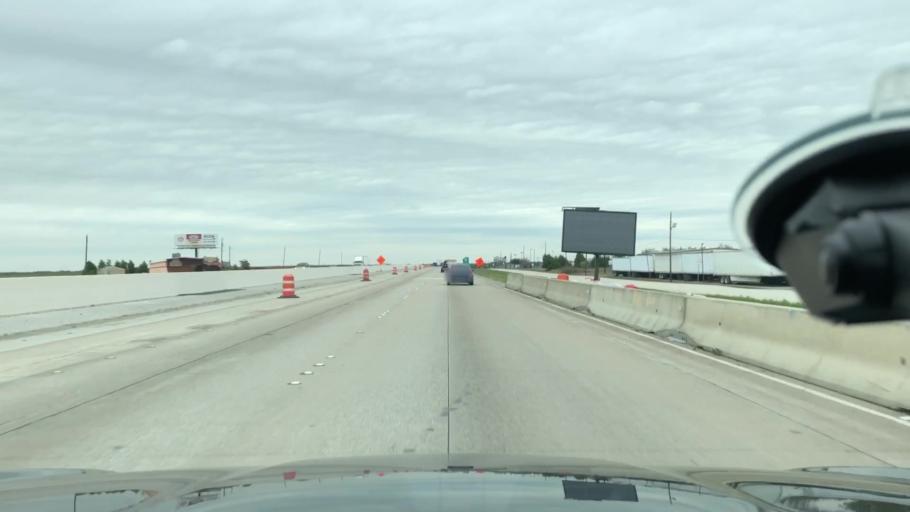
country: US
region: Texas
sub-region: Ellis County
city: Oak Leaf
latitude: 32.4795
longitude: -96.8330
